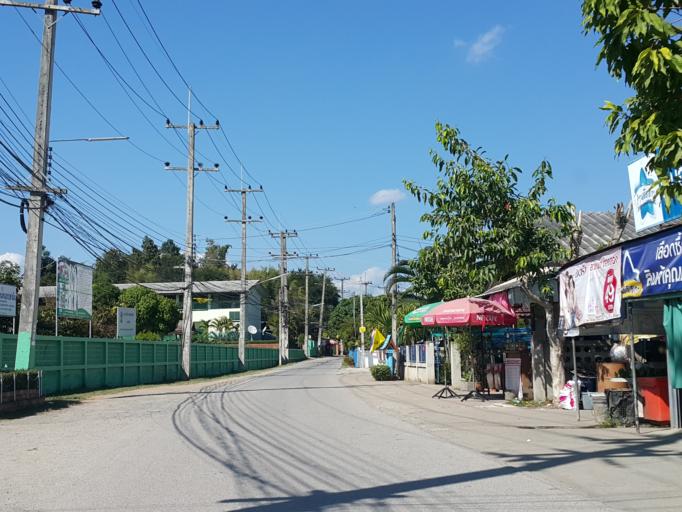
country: TH
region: Chiang Mai
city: Mae Taeng
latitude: 18.9585
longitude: 98.9193
